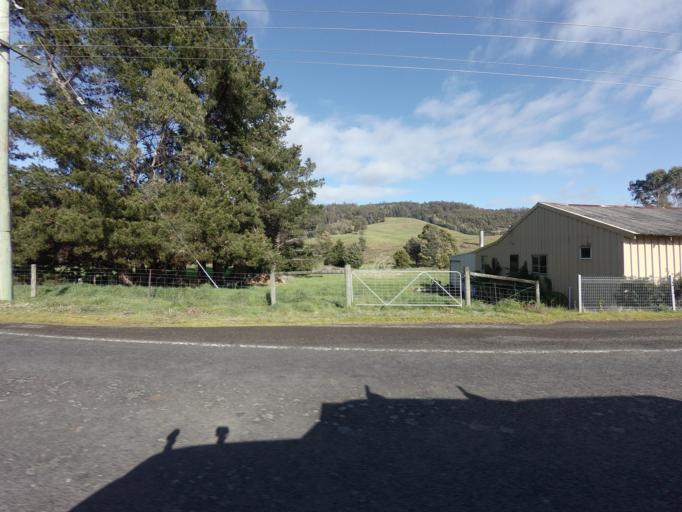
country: AU
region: Tasmania
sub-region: Huon Valley
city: Cygnet
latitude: -43.2940
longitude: 147.0114
